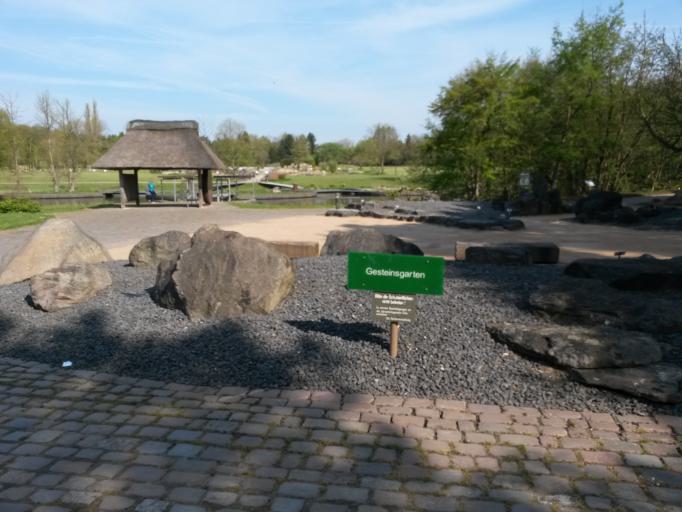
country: DE
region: Hamburg
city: Eidelstedt
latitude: 53.5618
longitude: 9.8630
